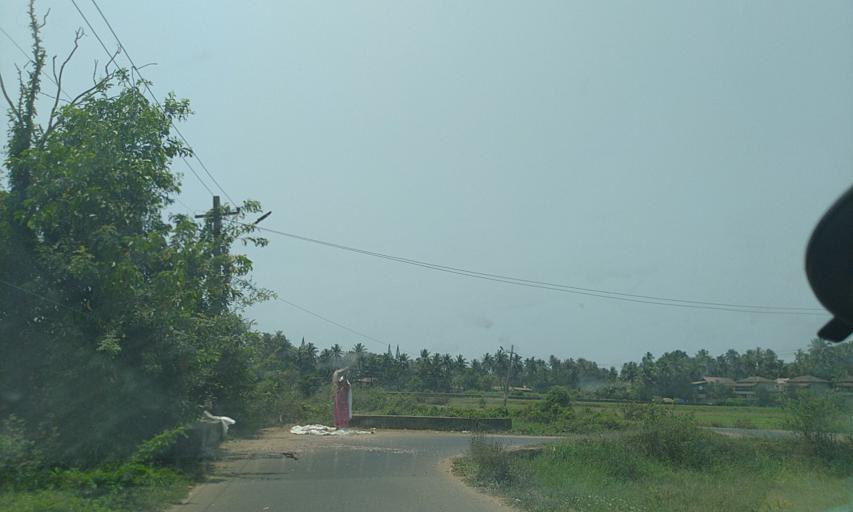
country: IN
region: Goa
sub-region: North Goa
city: Saligao
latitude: 15.5474
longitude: 73.7880
